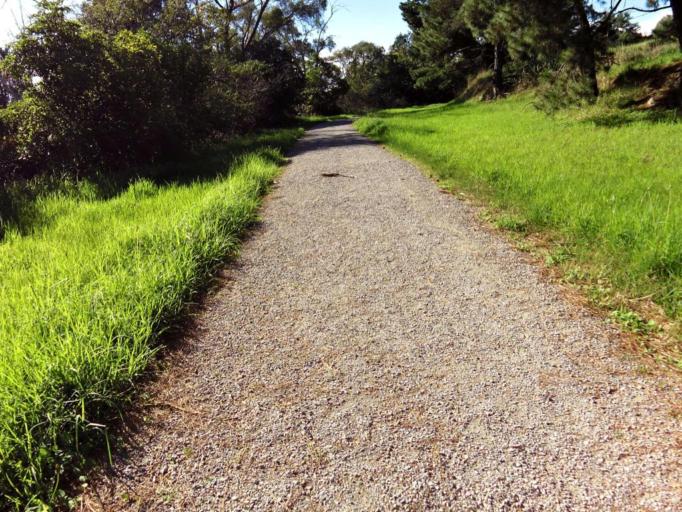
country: AU
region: Victoria
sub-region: Yarra Ranges
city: Mount Evelyn
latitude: -37.7839
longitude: 145.3671
